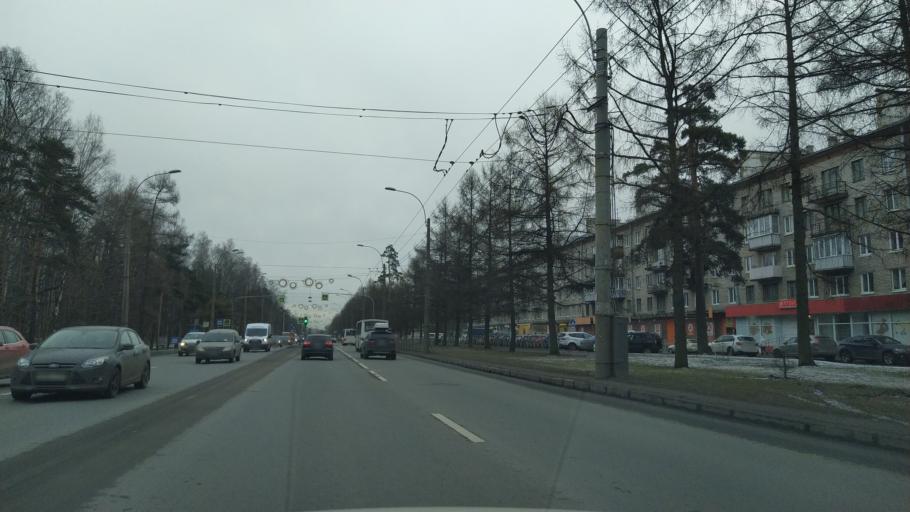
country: RU
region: St.-Petersburg
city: Sosnovka
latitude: 60.0172
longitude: 30.3367
